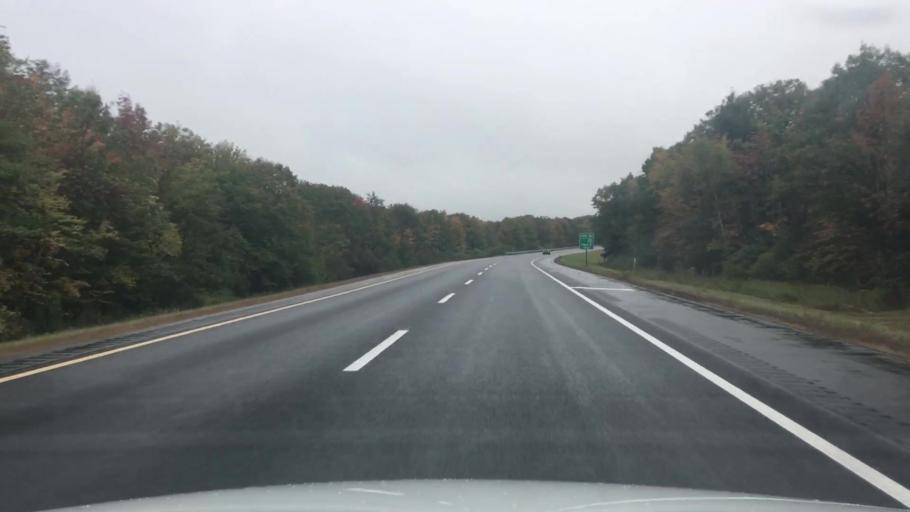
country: US
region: Maine
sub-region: Kennebec County
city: Gardiner
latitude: 44.1801
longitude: -69.8330
